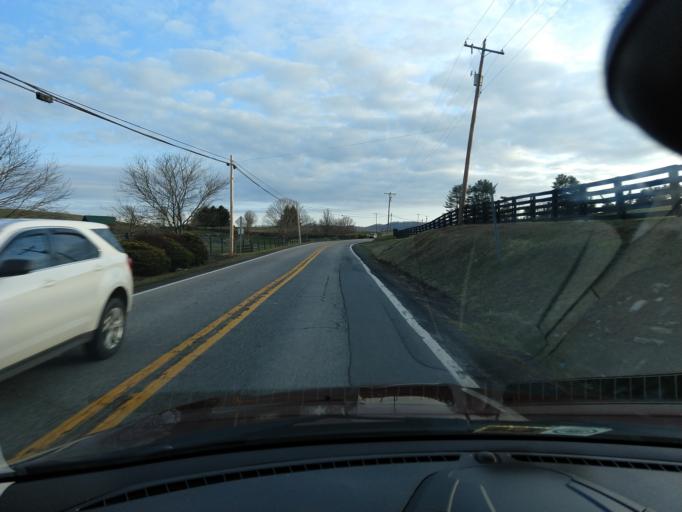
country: US
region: West Virginia
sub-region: Greenbrier County
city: Lewisburg
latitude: 37.9830
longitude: -80.3740
